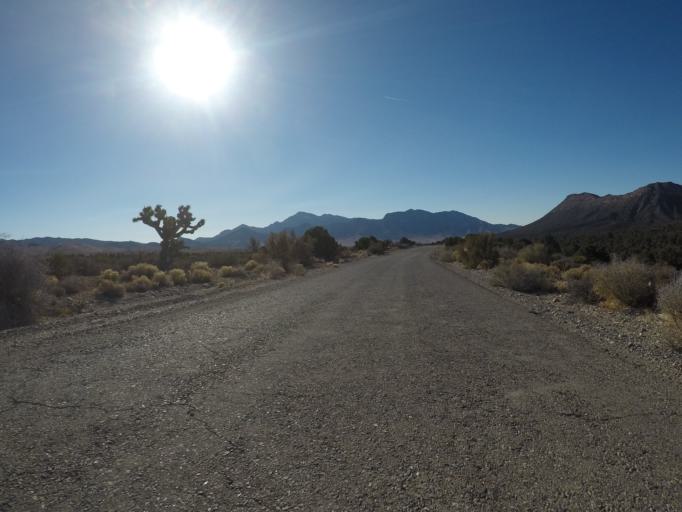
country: US
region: Nevada
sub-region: Clark County
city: Summerlin South
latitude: 36.0712
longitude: -115.5622
